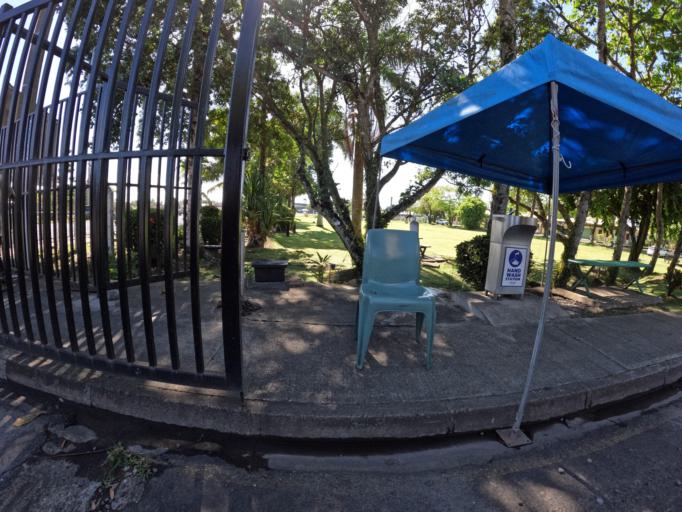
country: FJ
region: Central
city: Suva
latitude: -18.1480
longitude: 178.4476
